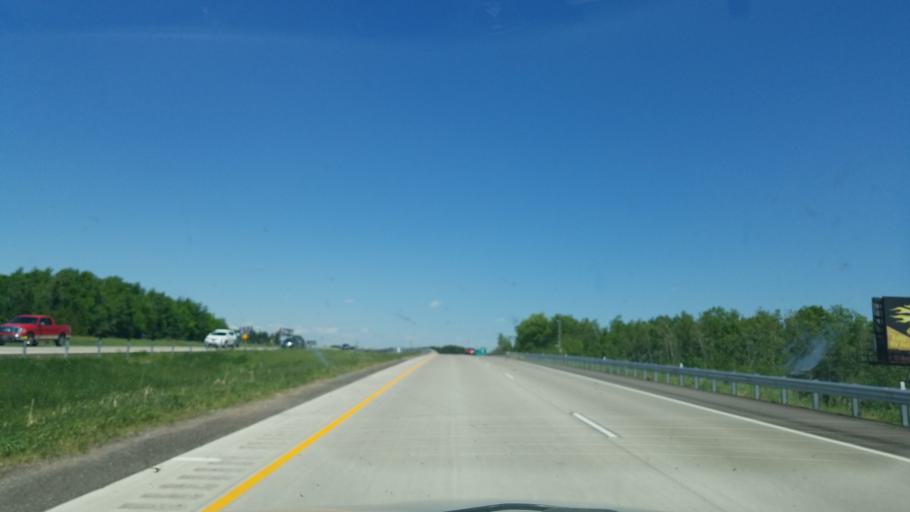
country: US
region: Minnesota
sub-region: Pine County
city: Hinckley
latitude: 45.9844
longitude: -92.9495
